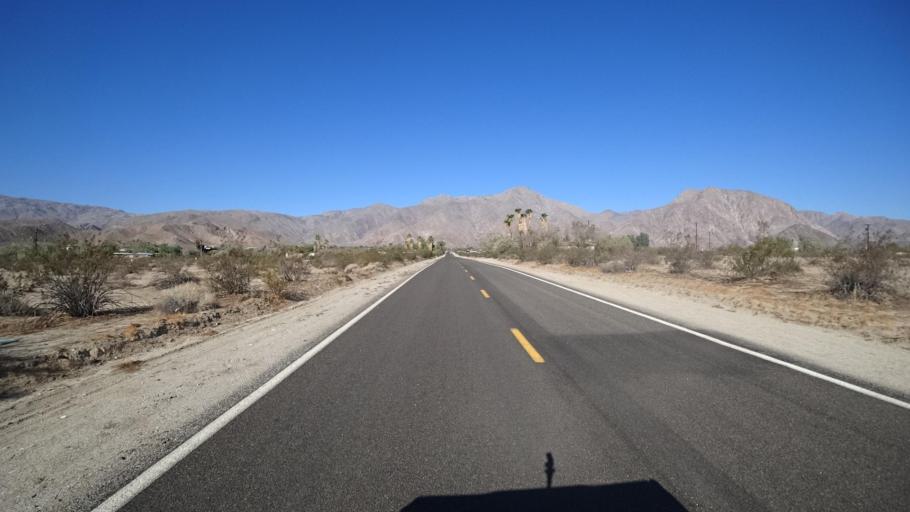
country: US
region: California
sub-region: San Diego County
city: Borrego Springs
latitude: 33.2593
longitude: -116.3771
